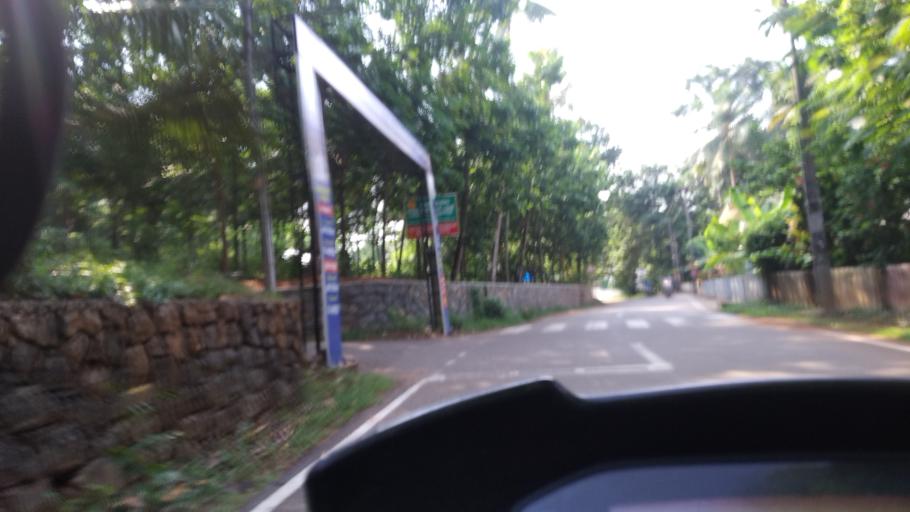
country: IN
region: Kerala
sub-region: Ernakulam
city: Piravam
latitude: 9.8544
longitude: 76.5268
